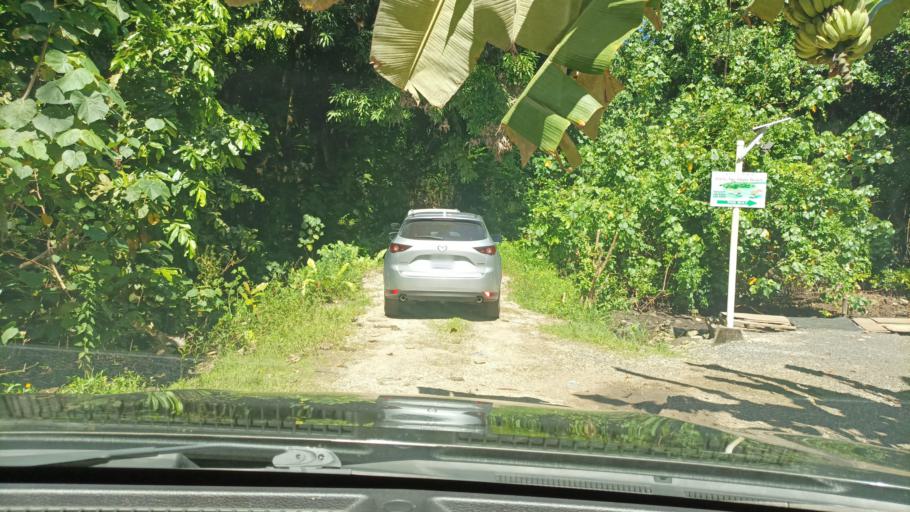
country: FM
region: Pohnpei
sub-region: Madolenihm Municipality
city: Madolenihm Municipality Government
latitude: 6.8429
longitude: 158.3208
